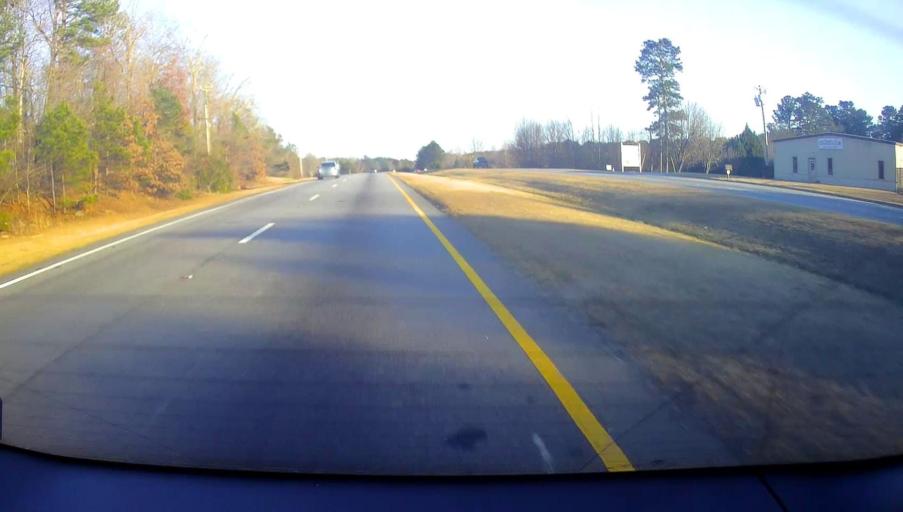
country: US
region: Georgia
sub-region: Fulton County
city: Fairburn
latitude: 33.5536
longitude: -84.5847
